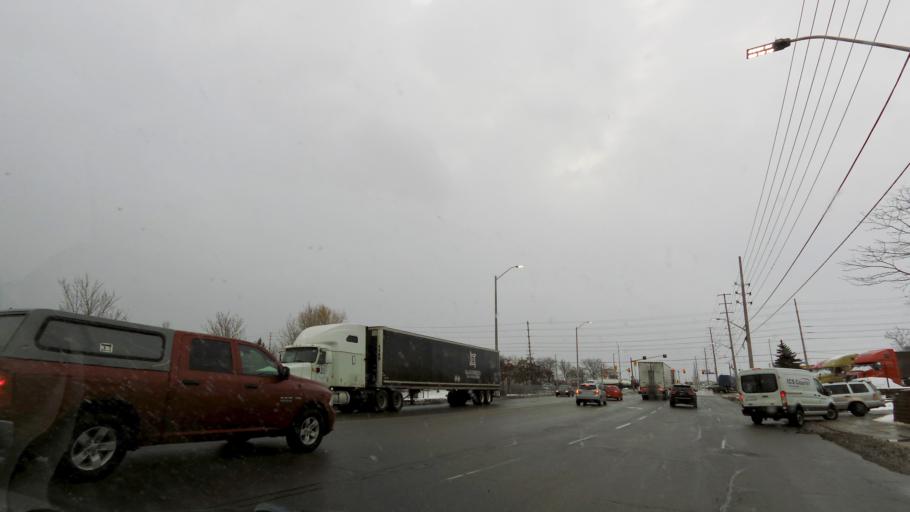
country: CA
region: Ontario
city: Mississauga
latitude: 43.6564
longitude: -79.6466
